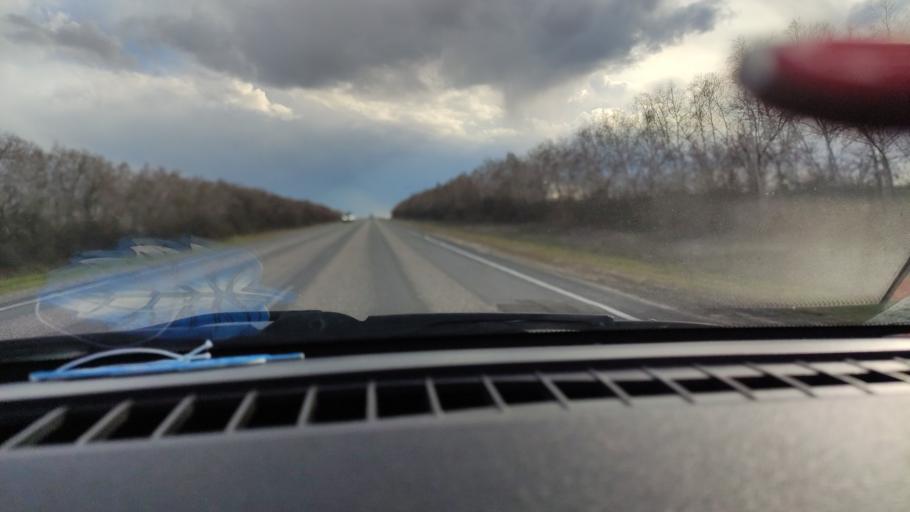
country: RU
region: Saratov
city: Sinodskoye
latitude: 51.9443
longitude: 46.6006
